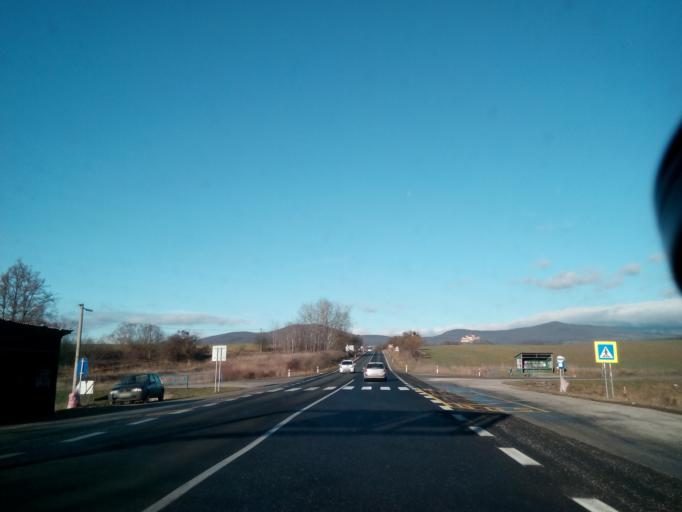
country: SK
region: Kosicky
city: Roznava
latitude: 48.6339
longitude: 20.6166
